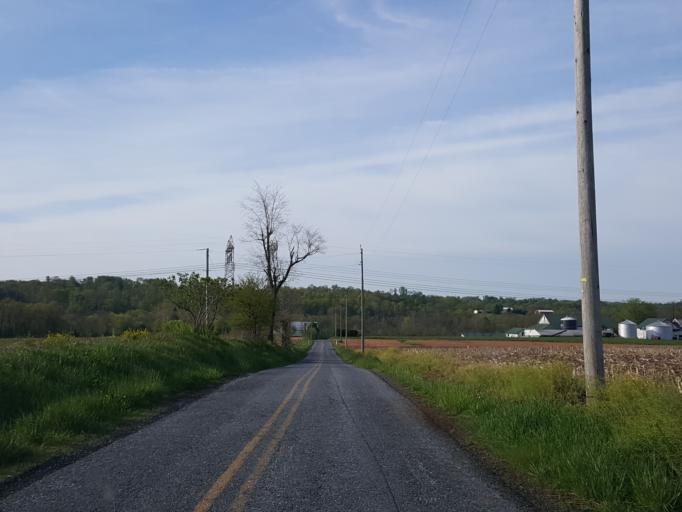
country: US
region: Pennsylvania
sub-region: Lancaster County
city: Elizabethtown
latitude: 40.2014
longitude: -76.5710
